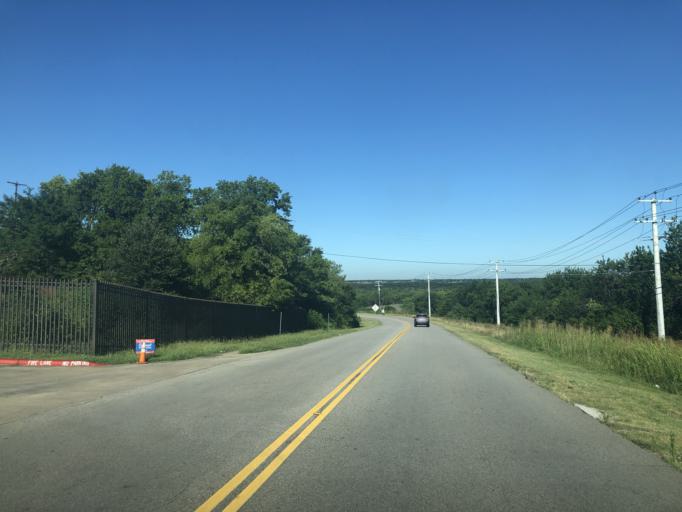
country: US
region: Texas
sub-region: Dallas County
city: Duncanville
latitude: 32.6618
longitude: -96.9670
